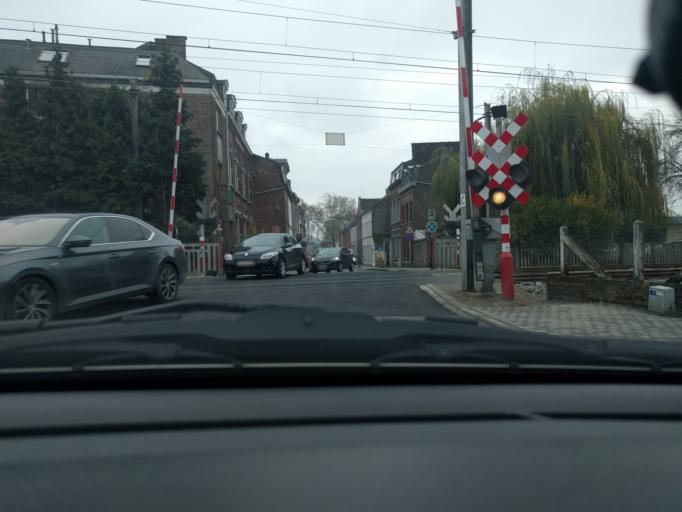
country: BE
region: Wallonia
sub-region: Province de Namur
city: Namur
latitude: 50.4684
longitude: 4.8817
